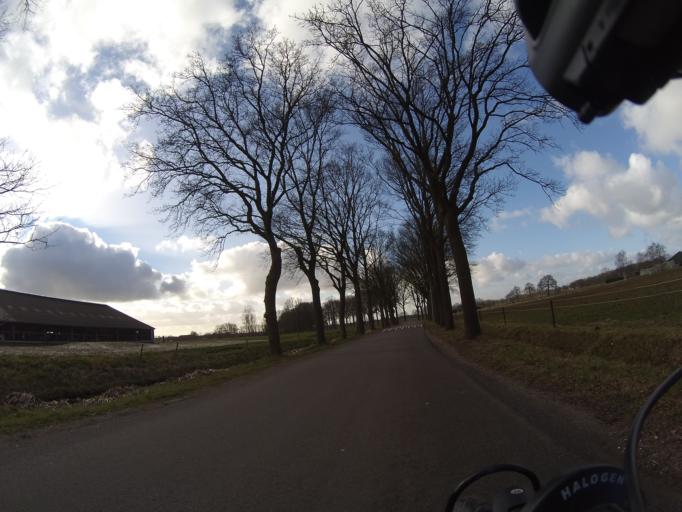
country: NL
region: Utrecht
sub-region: Gemeente Leusden
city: Leusden
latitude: 52.1631
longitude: 5.4588
